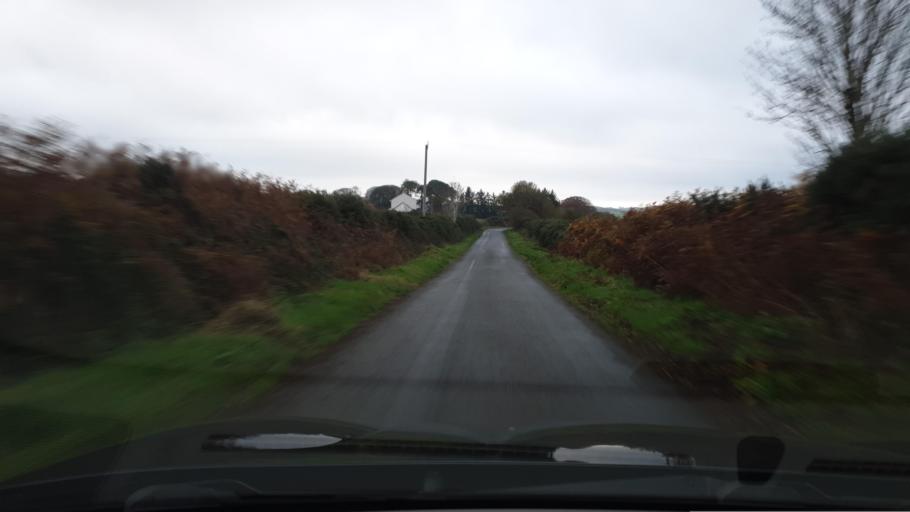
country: IE
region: Leinster
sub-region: Wicklow
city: Enniskerry
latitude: 53.1217
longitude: -6.1983
